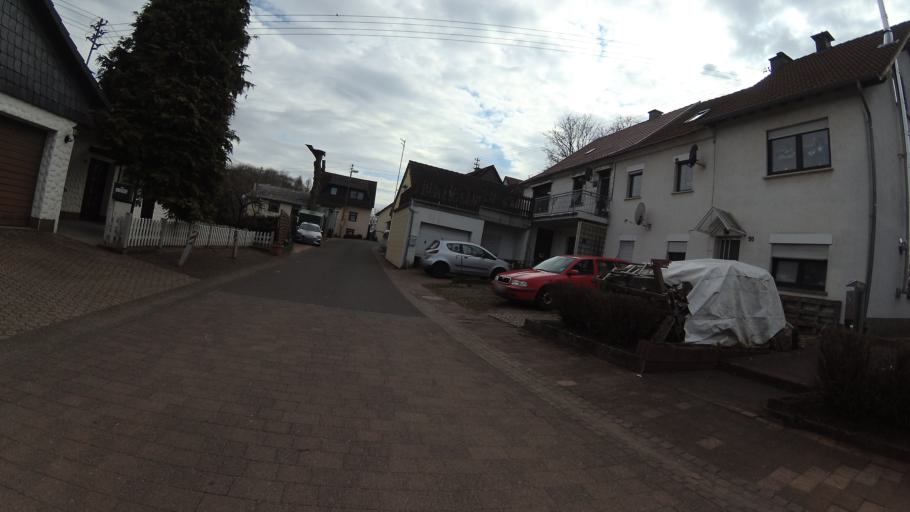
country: DE
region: Rheinland-Pfalz
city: Hahnweiler
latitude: 49.5720
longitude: 7.2213
